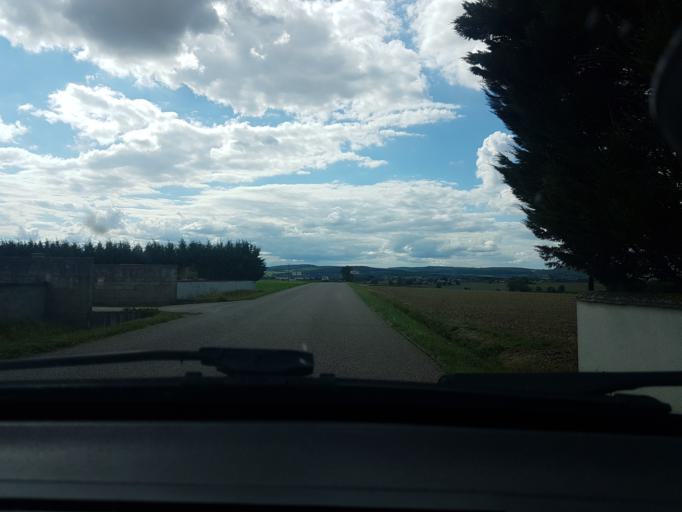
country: FR
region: Bourgogne
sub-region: Departement de Saone-et-Loire
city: Champforgeuil
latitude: 46.8430
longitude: 4.8088
